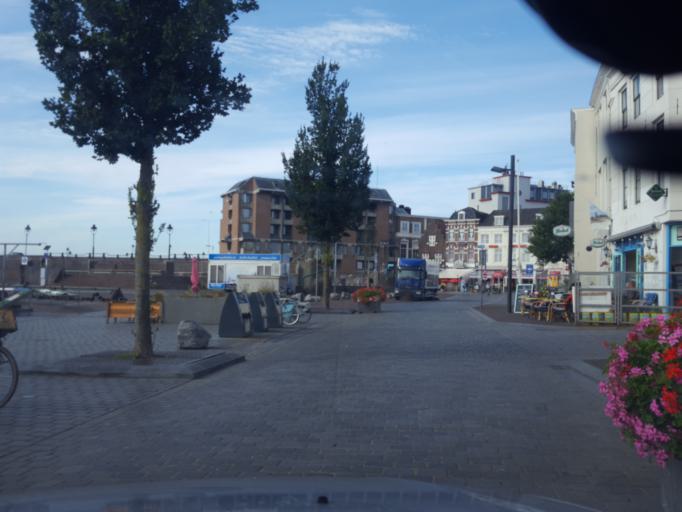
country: NL
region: Zeeland
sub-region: Gemeente Vlissingen
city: Vlissingen
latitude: 51.4411
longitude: 3.5752
